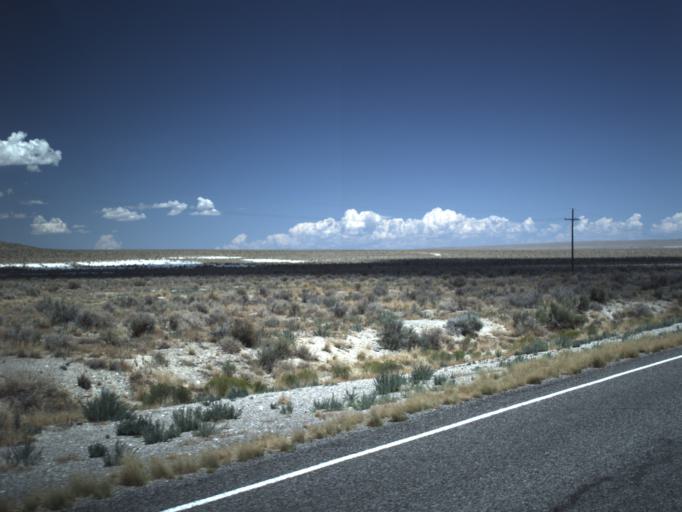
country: US
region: Utah
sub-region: Beaver County
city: Milford
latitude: 39.0628
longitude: -113.2404
